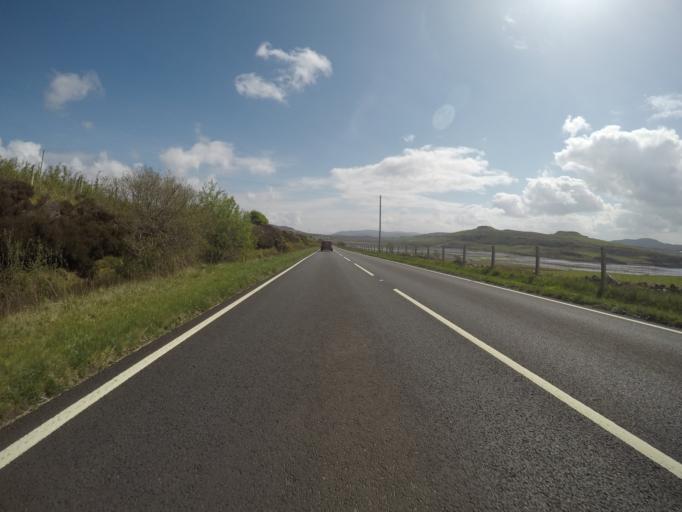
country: GB
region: Scotland
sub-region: Highland
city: Portree
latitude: 57.4919
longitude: -6.3183
